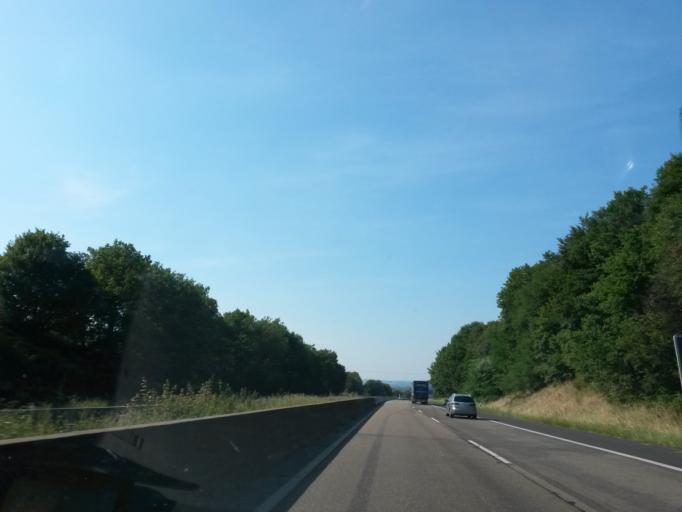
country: DE
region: Hesse
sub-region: Regierungsbezirk Kassel
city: Eichenzell
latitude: 50.4695
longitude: 9.7151
